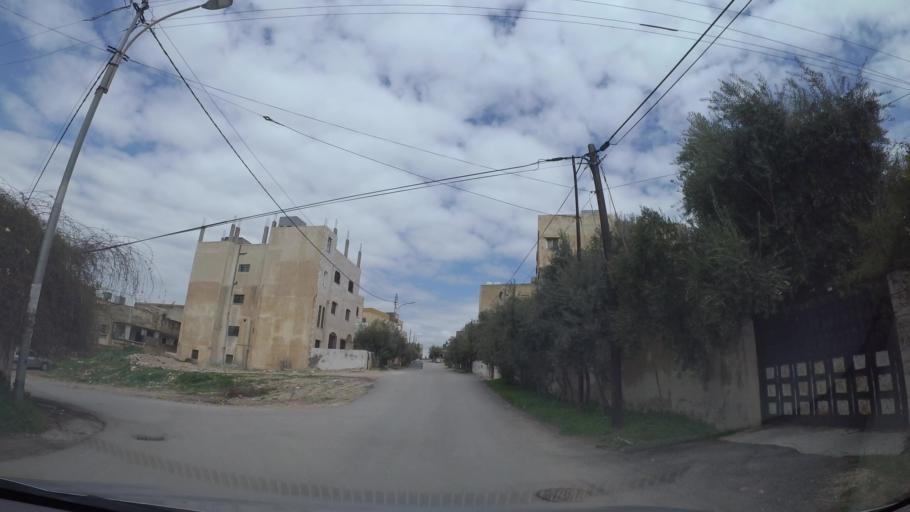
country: JO
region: Amman
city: Al Jubayhah
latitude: 32.0604
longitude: 35.8343
